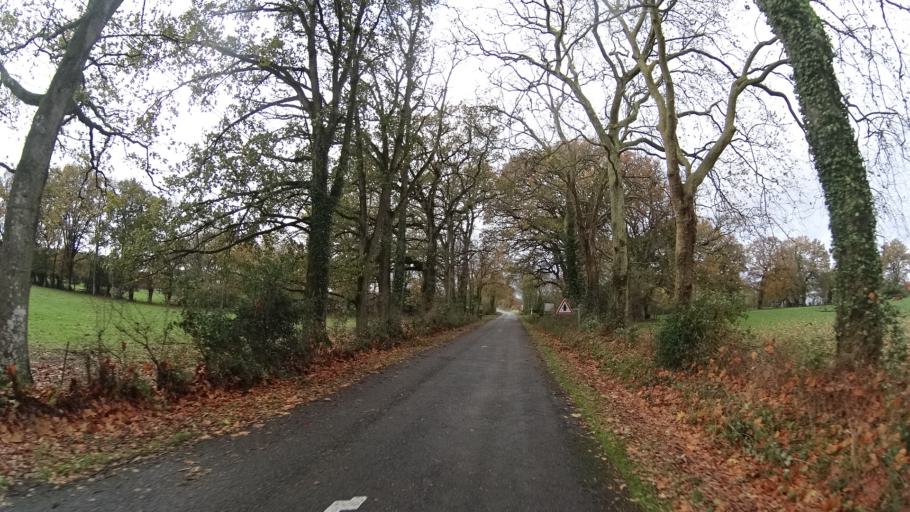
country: FR
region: Brittany
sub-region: Departement du Morbihan
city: Rieux
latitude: 47.5983
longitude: -2.0790
